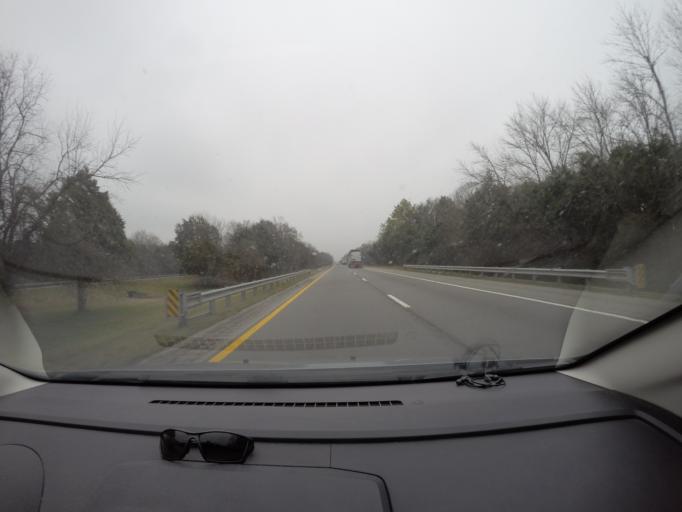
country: US
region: Tennessee
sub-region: Rutherford County
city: Plainview
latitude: 35.7397
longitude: -86.3347
